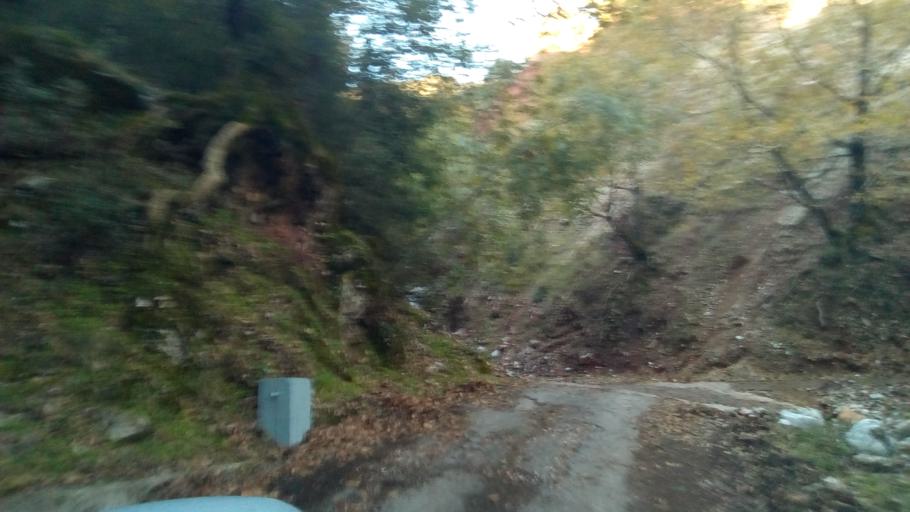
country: GR
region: West Greece
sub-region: Nomos Aitolias kai Akarnanias
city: Nafpaktos
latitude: 38.4657
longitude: 21.8687
